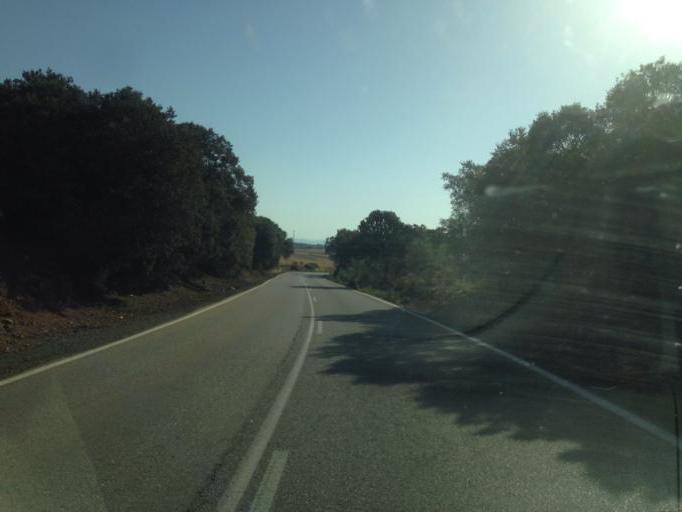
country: ES
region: Andalusia
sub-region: Provincia de Malaga
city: Villanueva de Tapia
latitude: 37.1169
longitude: -4.3134
